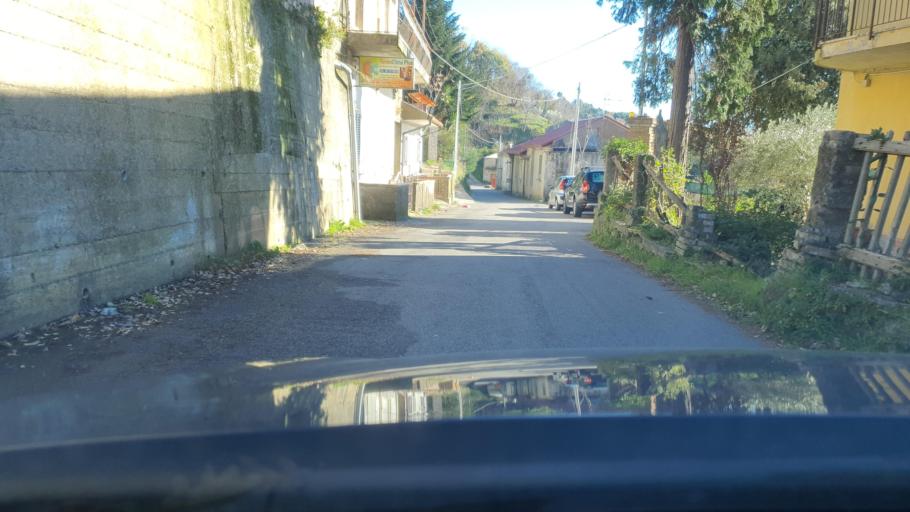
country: IT
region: Calabria
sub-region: Provincia di Catanzaro
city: Sant'Elia
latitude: 38.9584
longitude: 16.5787
